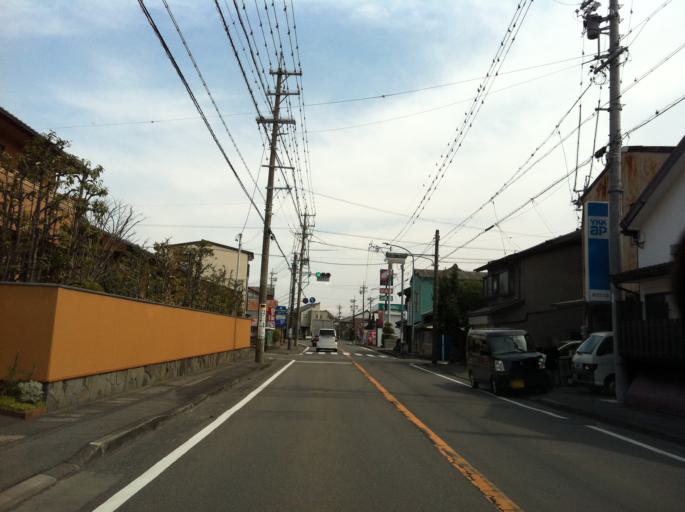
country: JP
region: Shizuoka
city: Fujieda
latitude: 34.8718
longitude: 138.2476
